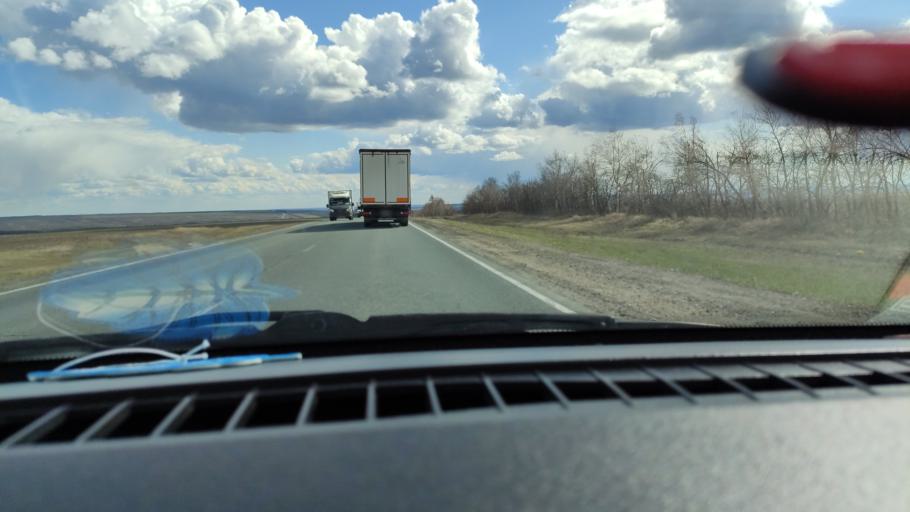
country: RU
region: Saratov
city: Dukhovnitskoye
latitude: 52.7867
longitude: 48.2325
